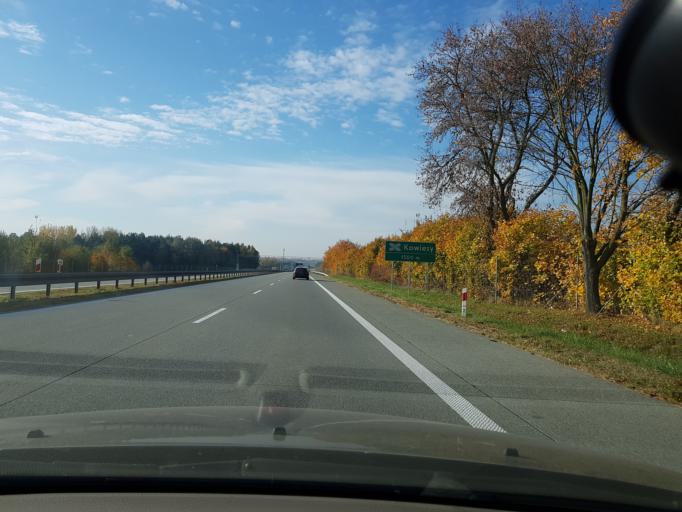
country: PL
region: Lodz Voivodeship
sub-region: Powiat skierniewicki
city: Kowiesy
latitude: 51.8993
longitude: 20.4313
